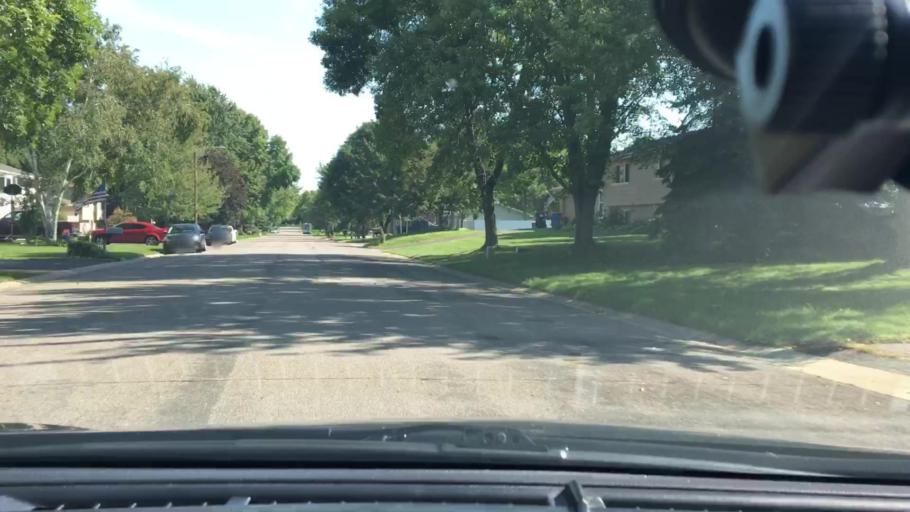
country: US
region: Minnesota
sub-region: Wright County
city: Saint Michael
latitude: 45.2024
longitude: -93.6743
